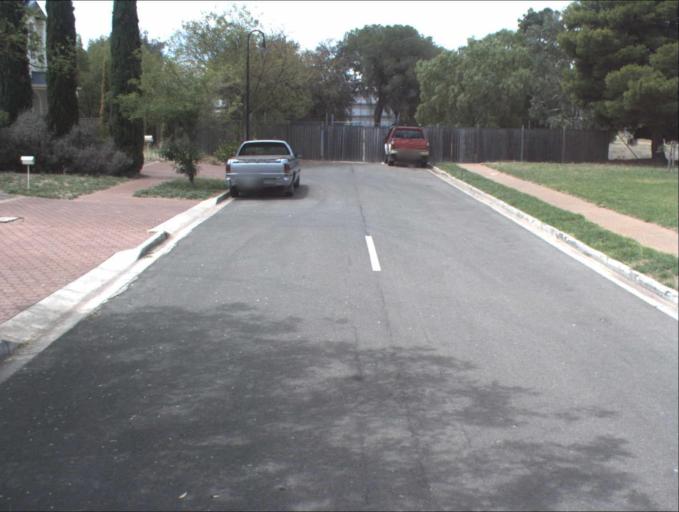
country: AU
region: South Australia
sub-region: Port Adelaide Enfield
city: Enfield
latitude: -34.8599
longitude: 138.6238
